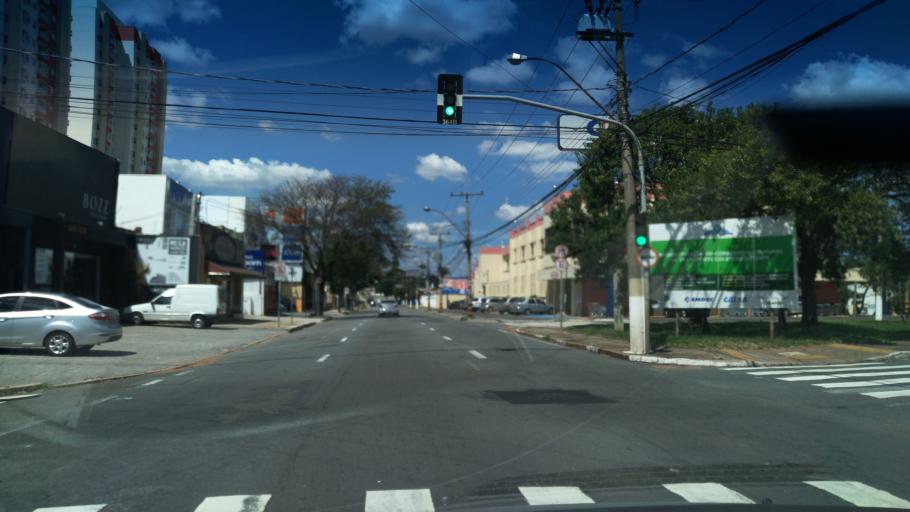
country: BR
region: Sao Paulo
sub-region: Campinas
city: Campinas
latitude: -22.9221
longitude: -47.0506
